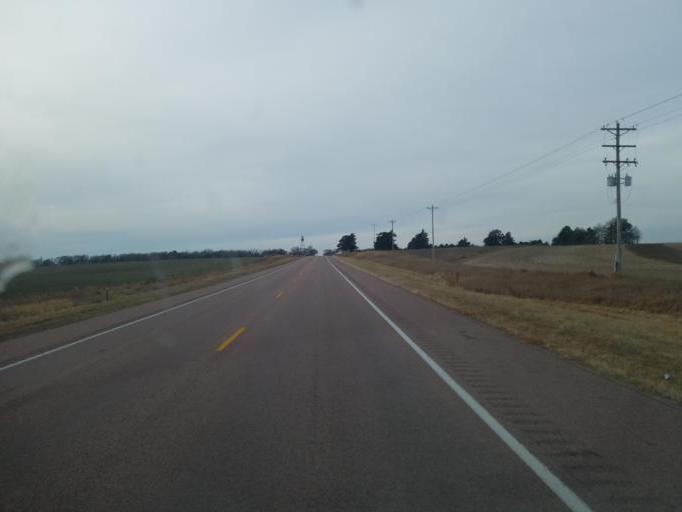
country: US
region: Nebraska
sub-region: Antelope County
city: Neligh
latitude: 42.3353
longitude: -98.1127
